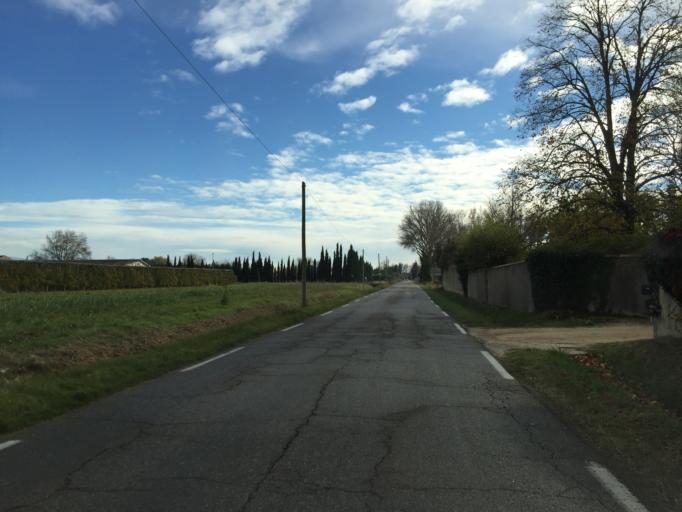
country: FR
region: Provence-Alpes-Cote d'Azur
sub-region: Departement du Vaucluse
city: Althen-des-Paluds
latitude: 43.9989
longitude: 4.9532
